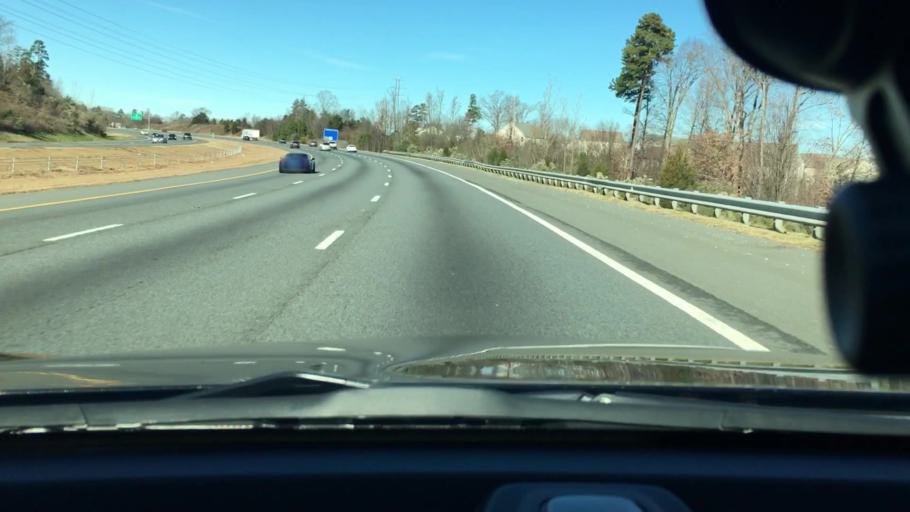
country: US
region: North Carolina
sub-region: Cabarrus County
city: Harrisburg
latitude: 35.3025
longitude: -80.6862
